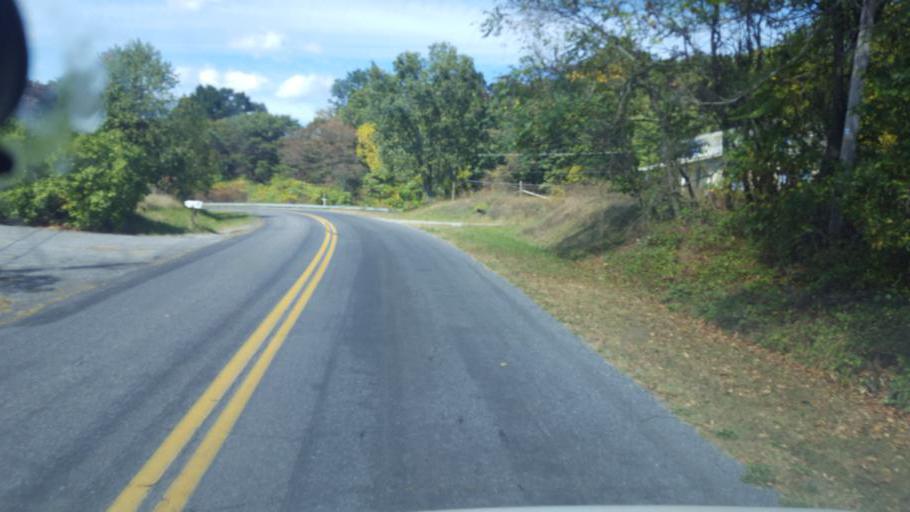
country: US
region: Virginia
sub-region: Rockingham County
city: Elkton
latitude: 38.4002
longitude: -78.5878
